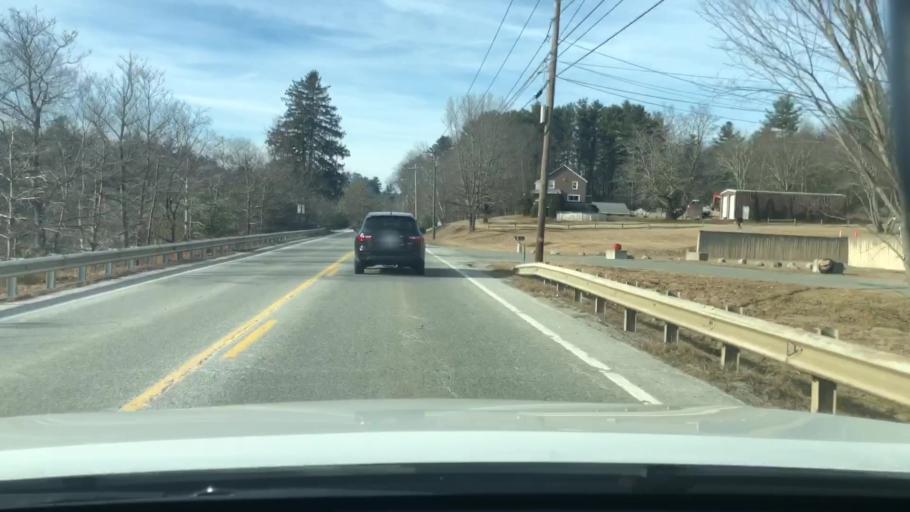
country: US
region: Massachusetts
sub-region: Worcester County
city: Northbridge
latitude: 42.1803
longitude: -71.6410
